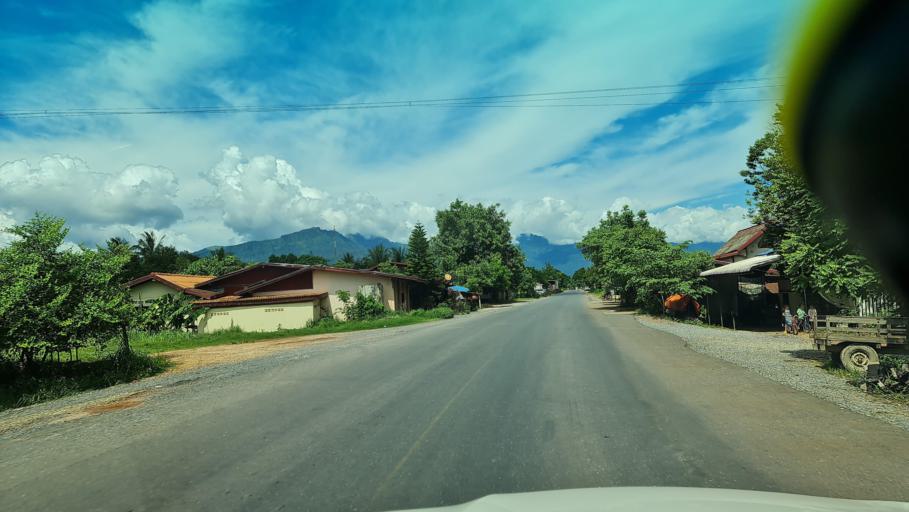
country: LA
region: Bolikhamxai
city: Pakkading
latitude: 18.2993
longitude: 104.0952
